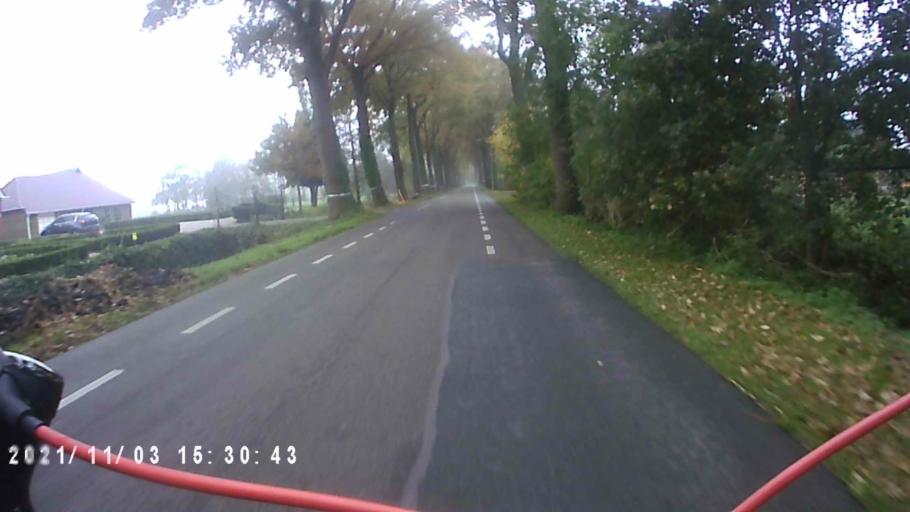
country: NL
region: Groningen
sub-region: Gemeente Leek
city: Leek
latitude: 53.1319
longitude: 6.3703
